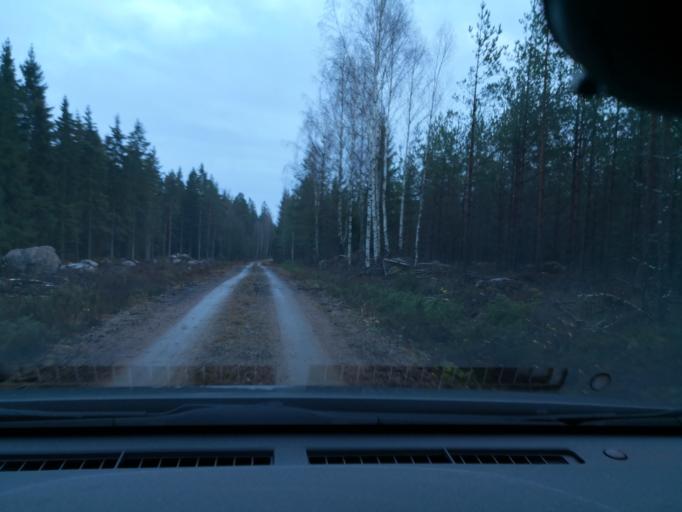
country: SE
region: Vaestmanland
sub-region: Hallstahammars Kommun
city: Hallstahammar
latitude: 59.5559
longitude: 16.1609
